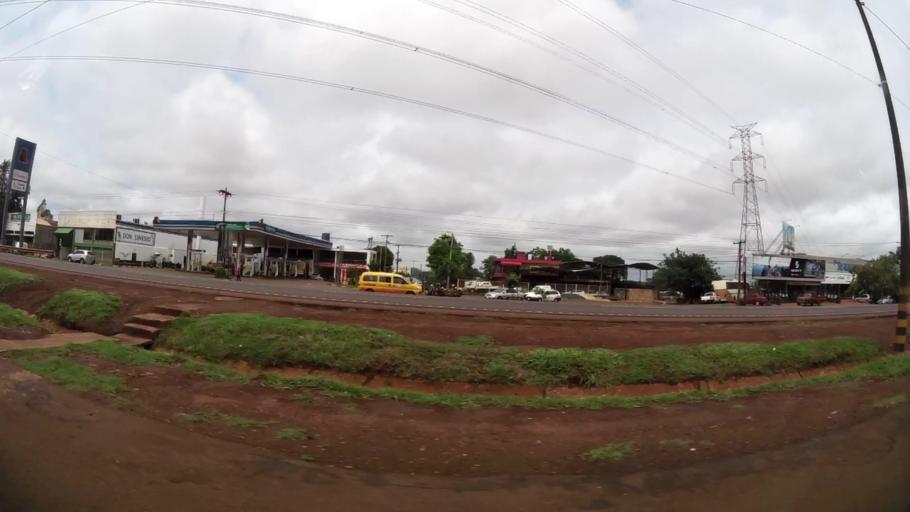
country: PY
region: Alto Parana
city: Ciudad del Este
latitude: -25.4957
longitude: -54.6874
